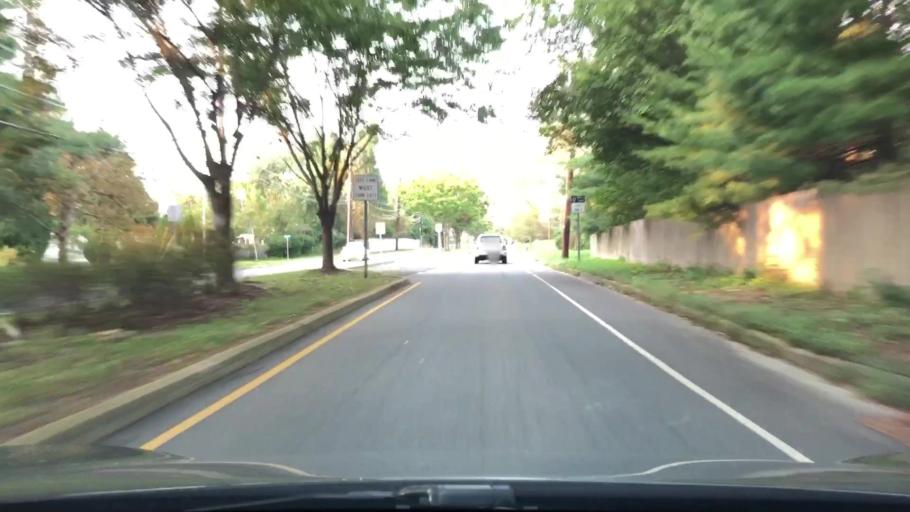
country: US
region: New Jersey
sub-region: Mercer County
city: Lawrenceville
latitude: 40.3002
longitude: -74.7521
